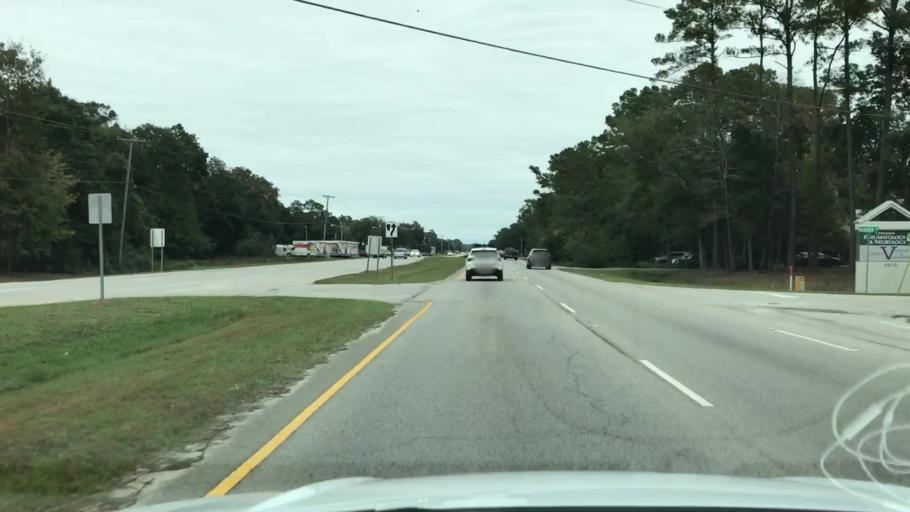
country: US
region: South Carolina
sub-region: Georgetown County
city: Murrells Inlet
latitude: 33.5432
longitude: -79.0527
